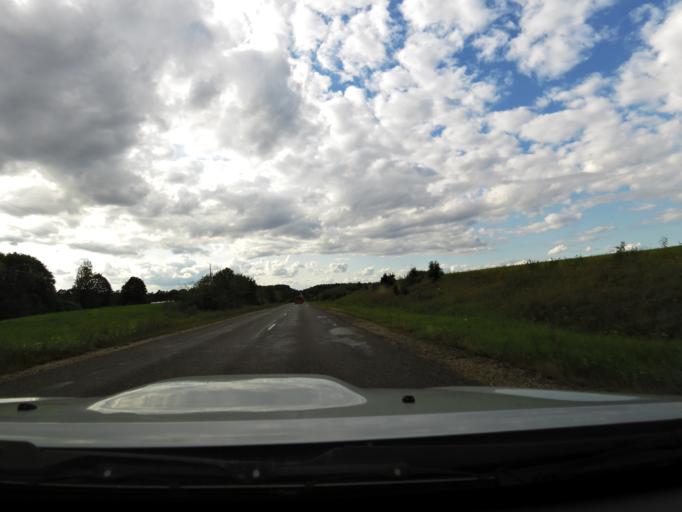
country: LV
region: Akniste
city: Akniste
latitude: 56.0005
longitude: 25.9572
